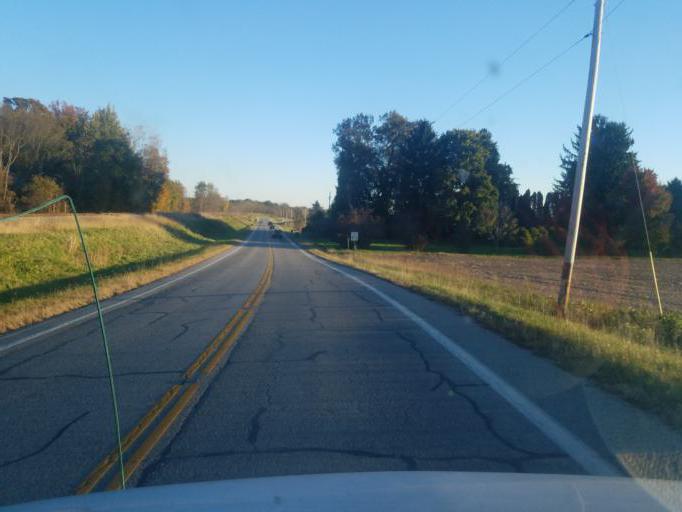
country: US
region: Ohio
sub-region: Licking County
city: Utica
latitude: 40.2994
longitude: -82.4553
